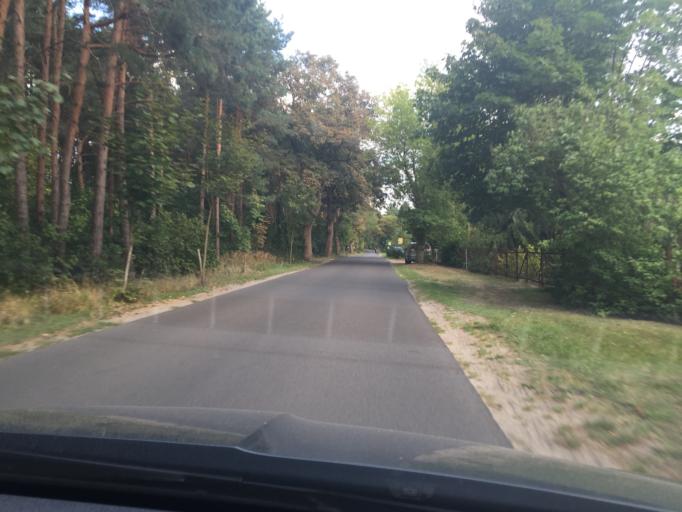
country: DE
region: Brandenburg
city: Erkner
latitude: 52.3758
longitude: 13.7772
